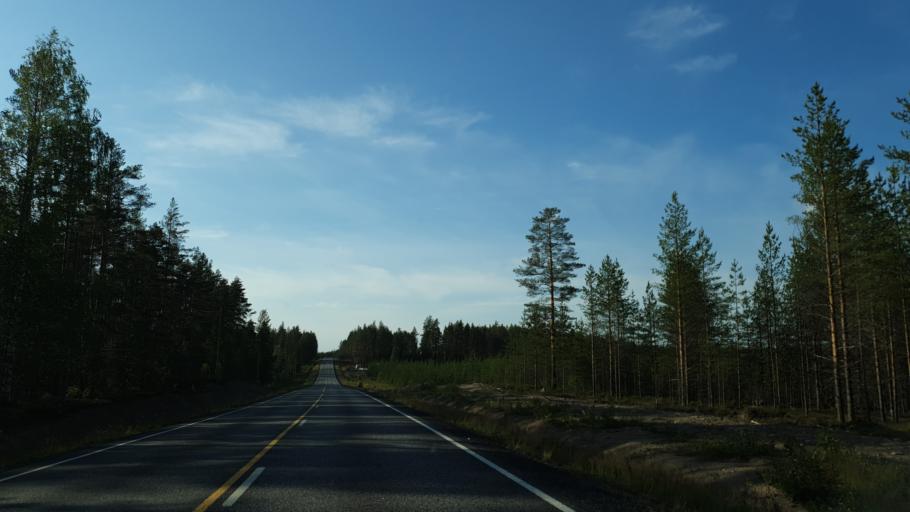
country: FI
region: Kainuu
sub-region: Kehys-Kainuu
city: Kuhmo
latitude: 64.0922
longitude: 29.4800
